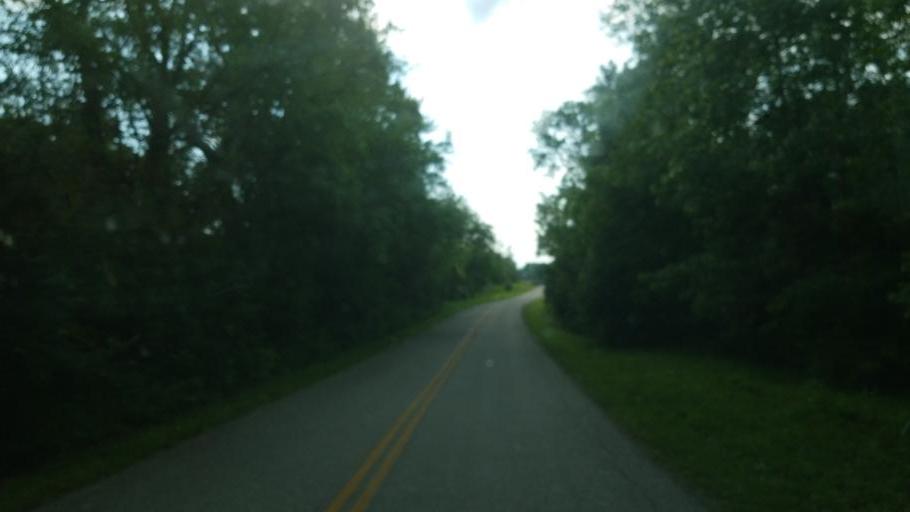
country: US
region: Ohio
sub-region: Knox County
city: Centerburg
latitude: 40.3214
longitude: -82.7677
